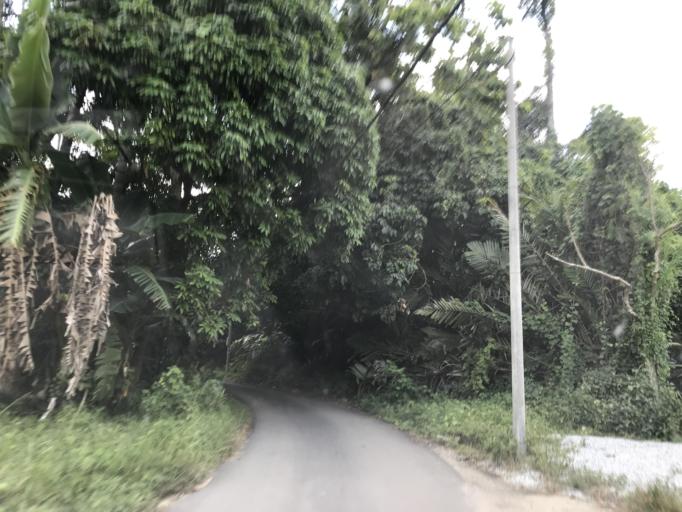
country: MY
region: Kelantan
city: Kota Bharu
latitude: 6.1118
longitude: 102.1874
